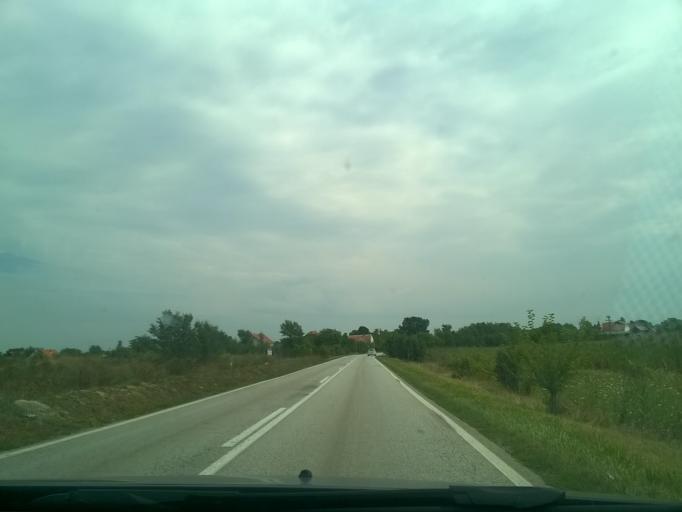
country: RS
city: Sutjeska
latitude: 45.3805
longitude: 20.6874
